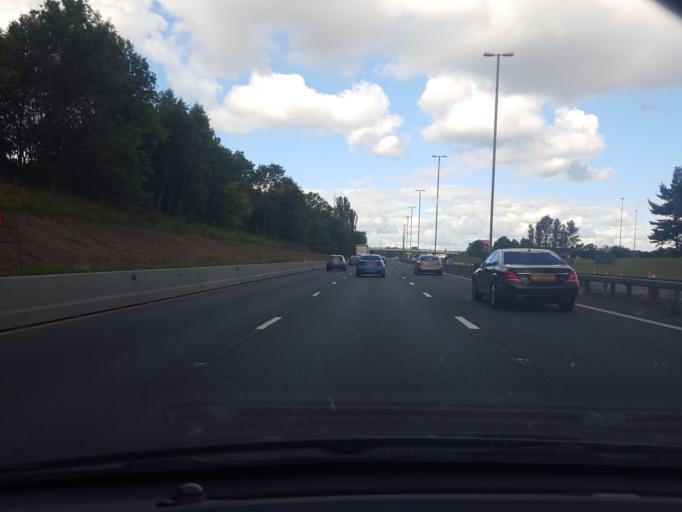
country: GB
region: Scotland
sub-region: South Lanarkshire
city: Bothwell
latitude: 55.8113
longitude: -4.0619
